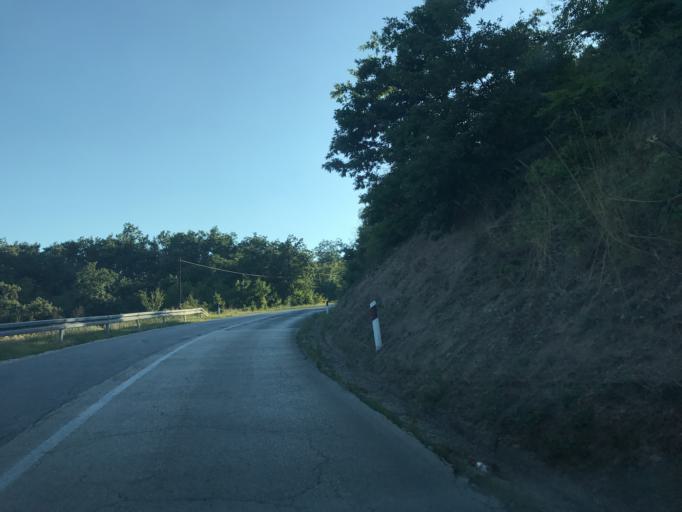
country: RO
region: Mehedinti
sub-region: Comuna Svinita
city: Svinita
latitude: 44.3006
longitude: 22.2583
